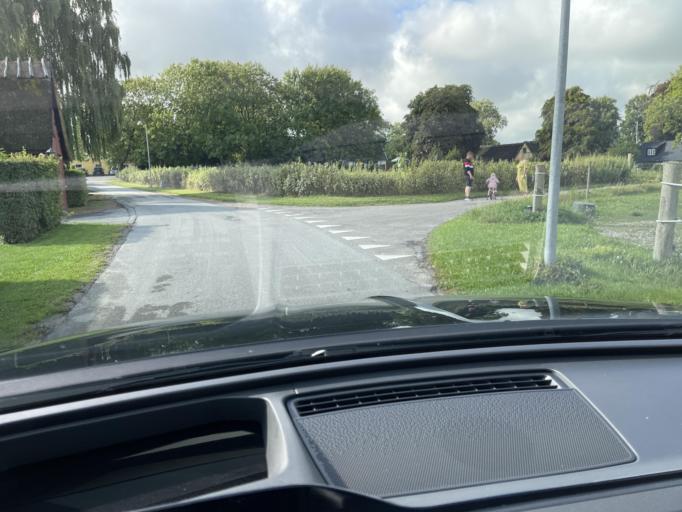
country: DK
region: Zealand
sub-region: Solrod Kommune
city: Havdrup
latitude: 55.5659
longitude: 12.1115
